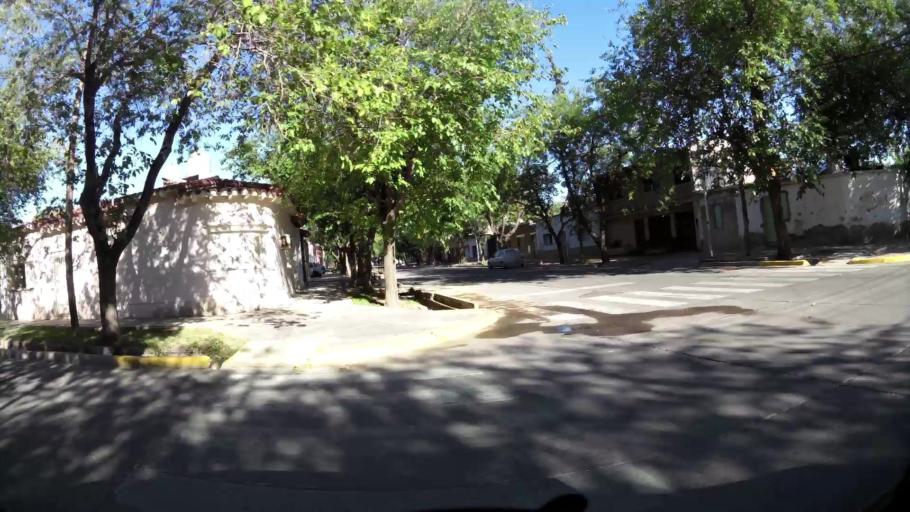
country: AR
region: Mendoza
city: Las Heras
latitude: -32.8669
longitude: -68.8359
